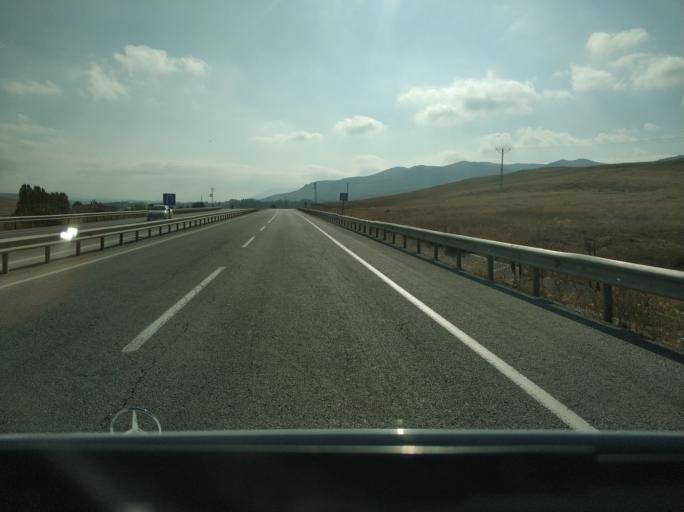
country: TR
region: Sivas
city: Yildizeli
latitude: 39.8357
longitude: 36.4421
